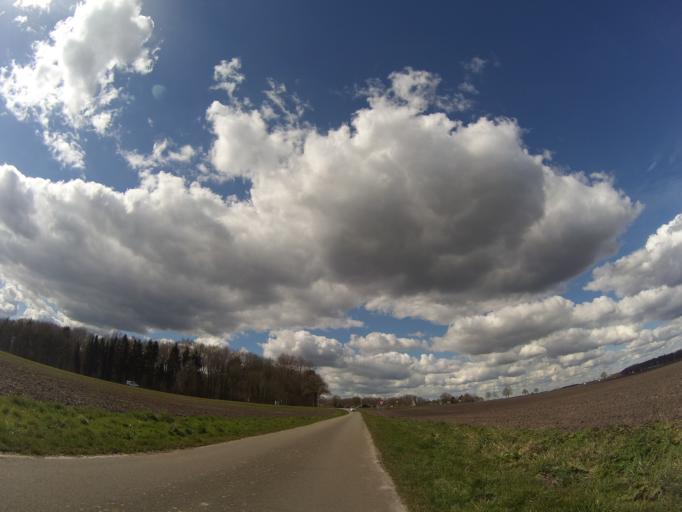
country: NL
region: Drenthe
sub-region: Gemeente Coevorden
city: Sleen
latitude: 52.7783
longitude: 6.8082
